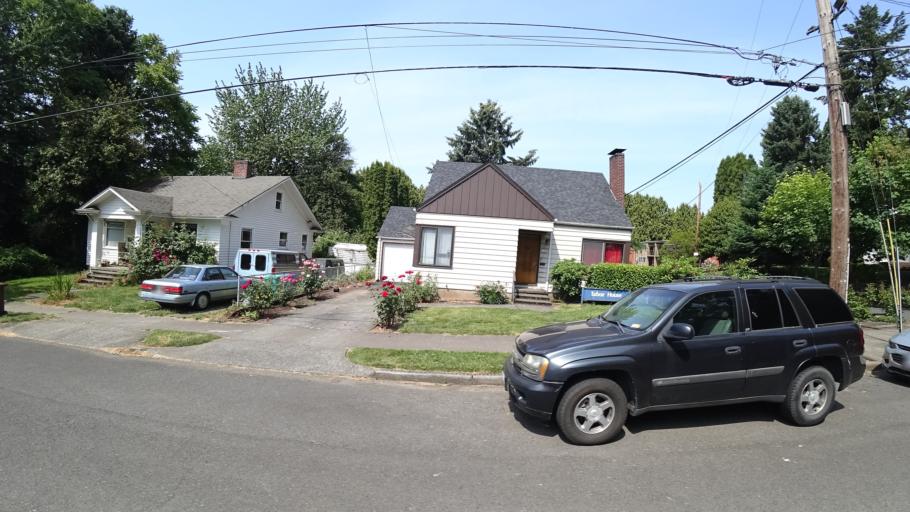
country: US
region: Oregon
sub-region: Multnomah County
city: Lents
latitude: 45.5066
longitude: -122.5952
